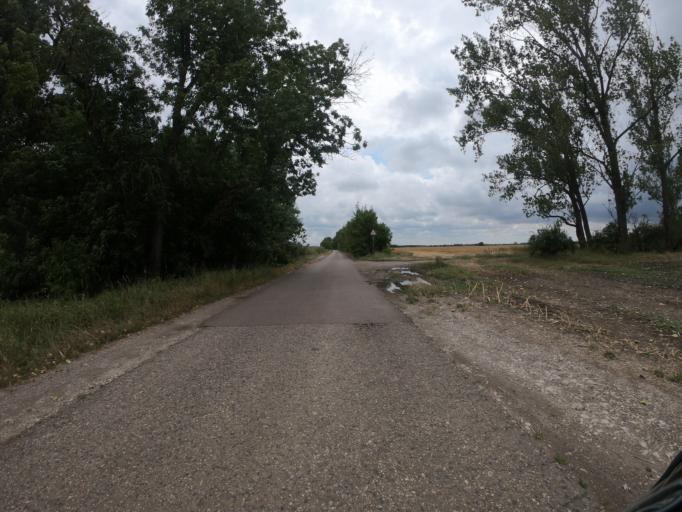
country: HU
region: Borsod-Abauj-Zemplen
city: Szentistvan
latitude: 47.7398
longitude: 20.6815
